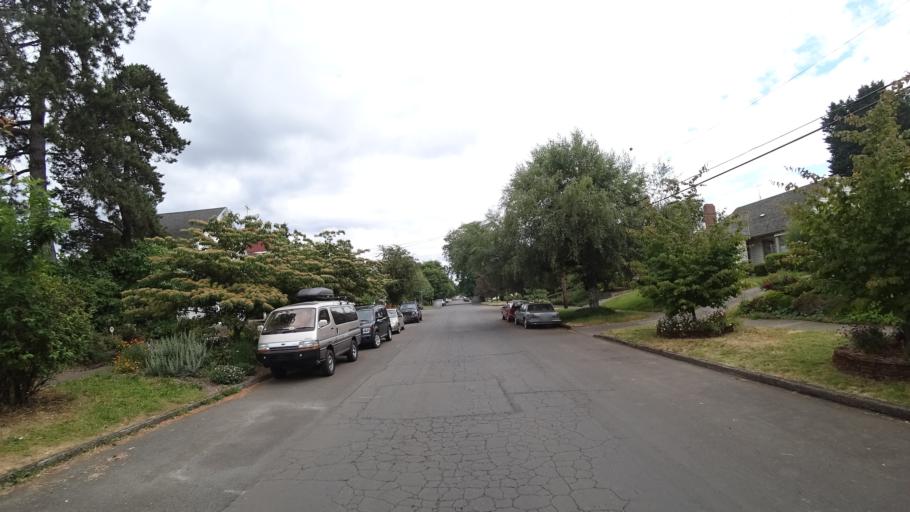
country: US
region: Oregon
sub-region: Washington County
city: West Haven
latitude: 45.5791
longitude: -122.7338
